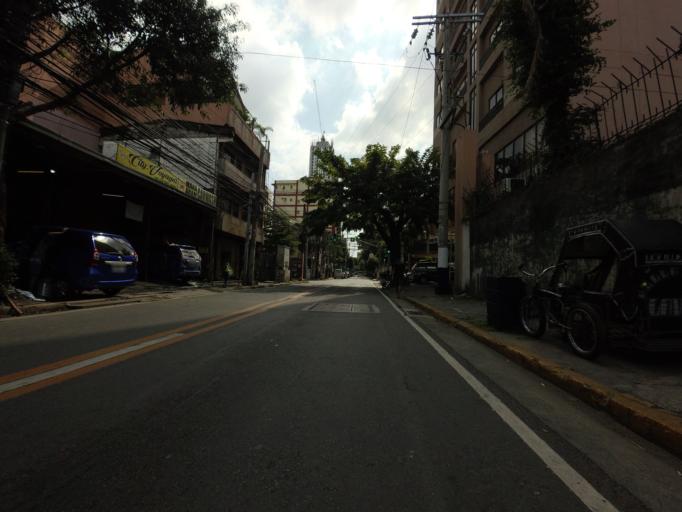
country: PH
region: Metro Manila
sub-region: City of Manila
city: Port Area
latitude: 14.5659
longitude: 120.9969
